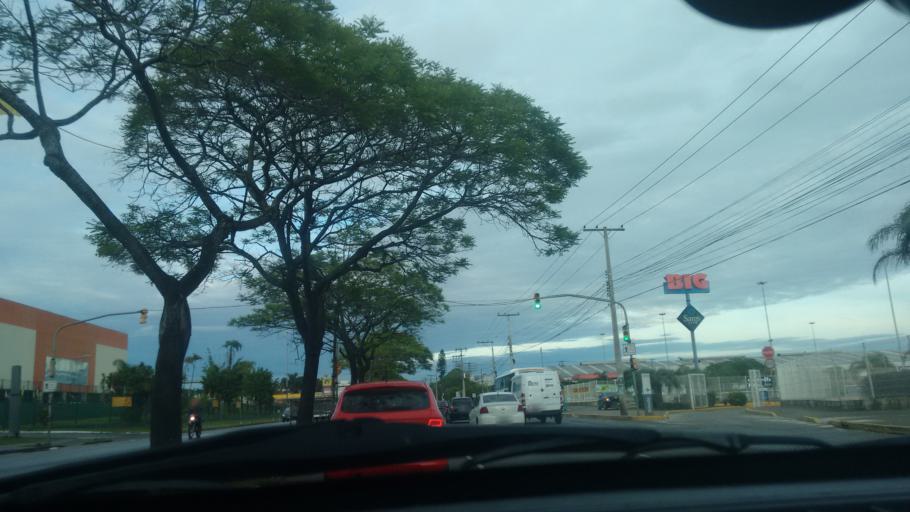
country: BR
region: Rio Grande do Sul
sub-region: Cachoeirinha
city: Cachoeirinha
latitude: -29.9978
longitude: -51.1408
